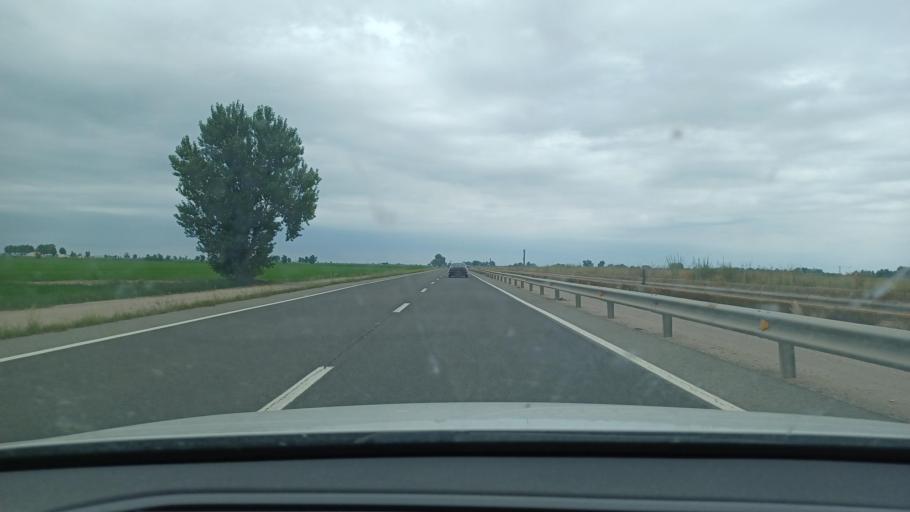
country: ES
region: Catalonia
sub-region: Provincia de Tarragona
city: Amposta
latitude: 40.7137
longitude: 0.6219
